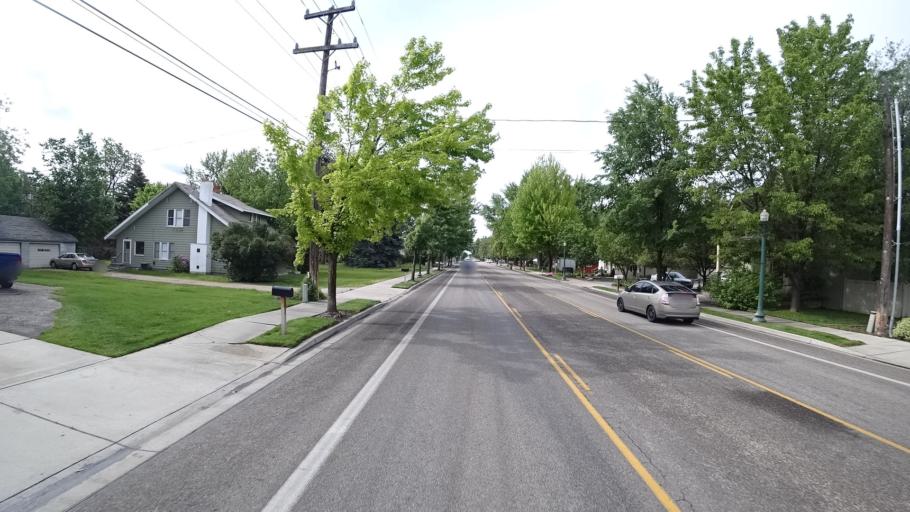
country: US
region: Idaho
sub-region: Ada County
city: Eagle
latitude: 43.6971
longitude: -116.3540
